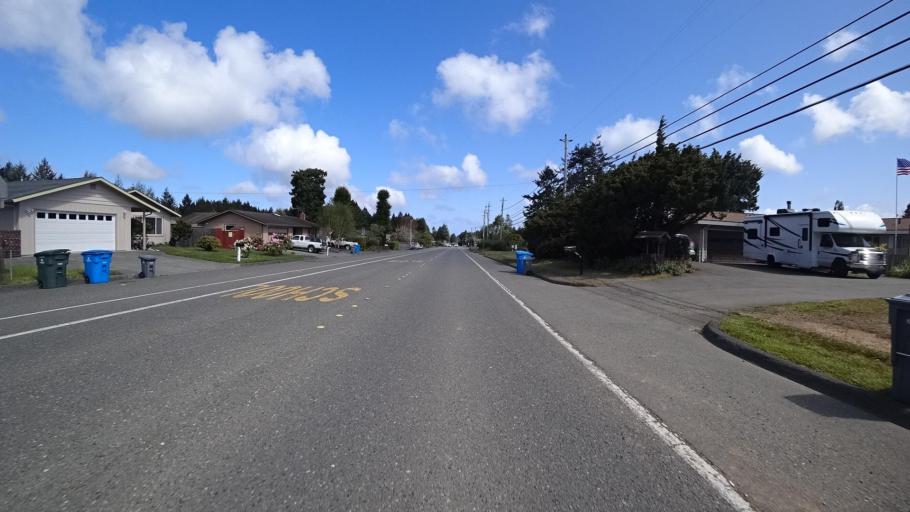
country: US
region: California
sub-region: Humboldt County
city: Pine Hills
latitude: 40.7385
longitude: -124.1475
